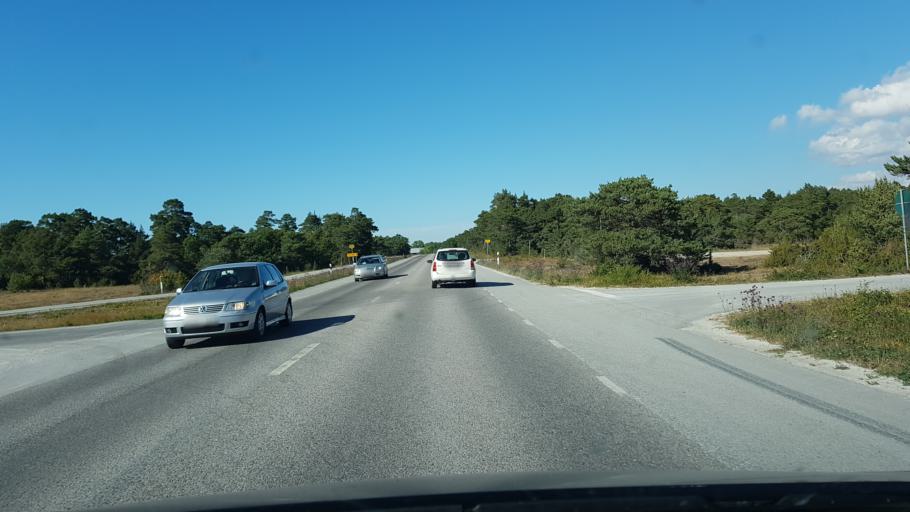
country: SE
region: Gotland
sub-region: Gotland
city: Vibble
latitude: 57.5639
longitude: 18.2053
